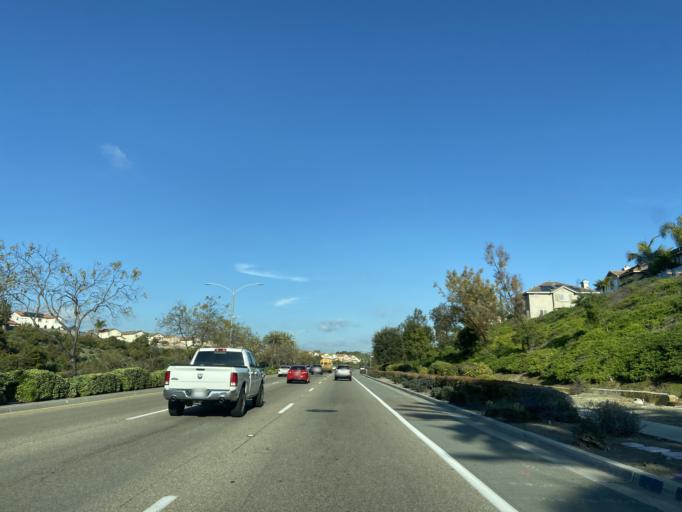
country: US
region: California
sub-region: San Diego County
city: Bonita
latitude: 32.6307
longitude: -116.9775
